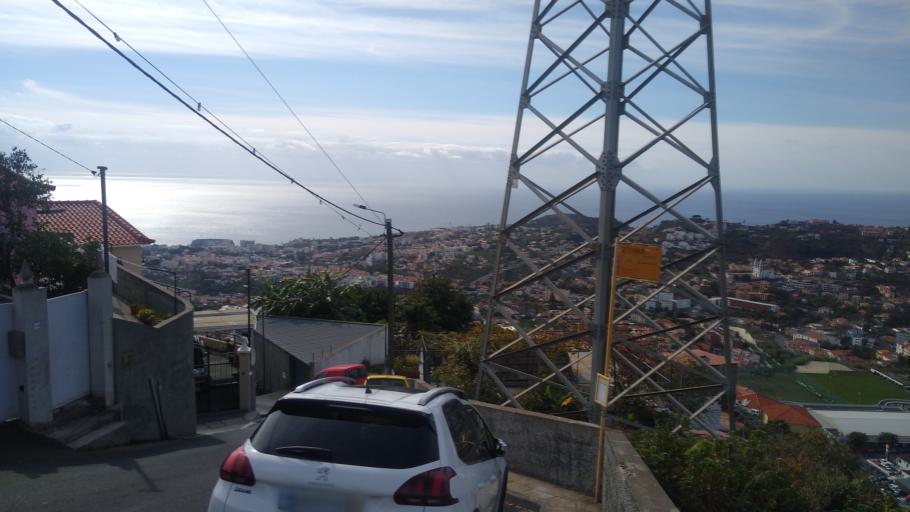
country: PT
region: Madeira
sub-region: Funchal
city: Nossa Senhora do Monte
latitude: 32.6747
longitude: -16.9333
